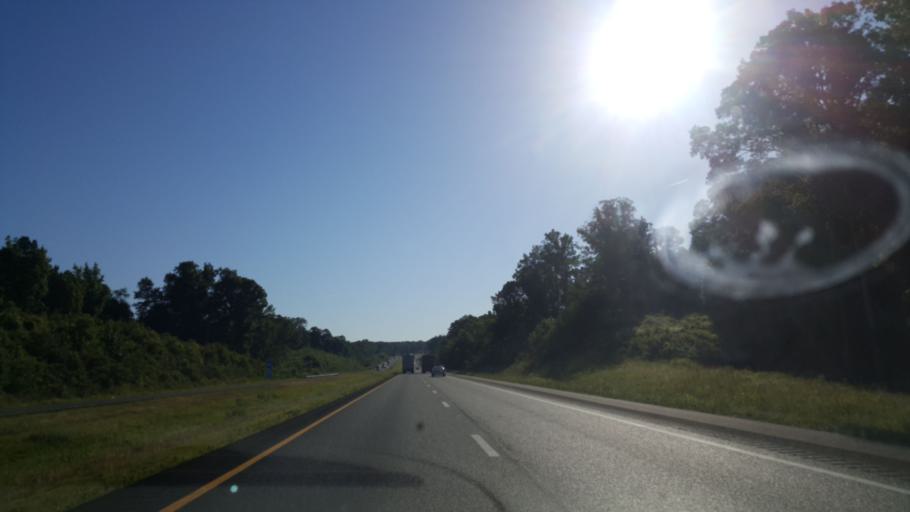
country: US
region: Tennessee
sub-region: Humphreys County
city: New Johnsonville
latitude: 35.8632
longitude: -88.0437
